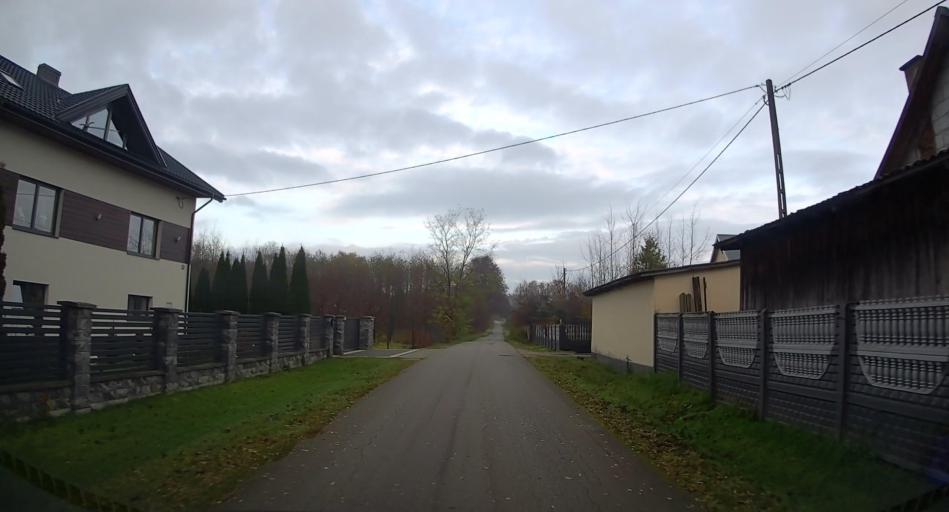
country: PL
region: Lodz Voivodeship
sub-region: Powiat skierniewicki
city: Kowiesy
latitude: 51.9343
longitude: 20.4024
